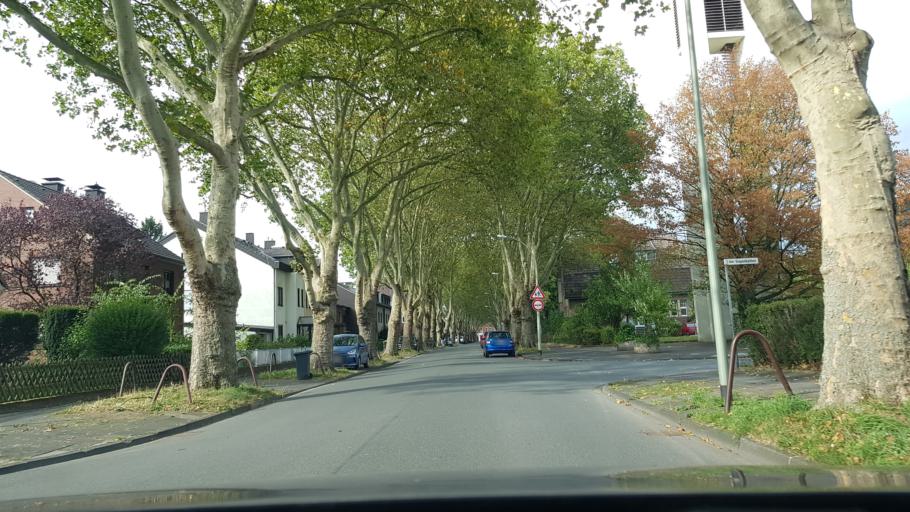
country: DE
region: North Rhine-Westphalia
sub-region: Regierungsbezirk Dusseldorf
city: Hochfeld
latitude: 51.3622
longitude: 6.7816
